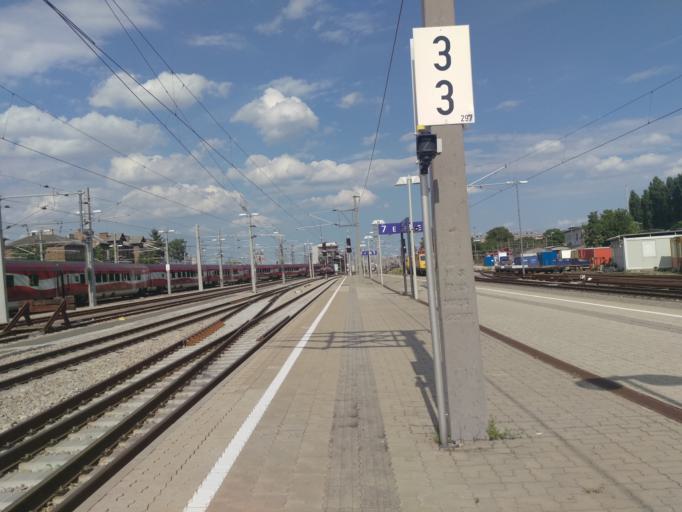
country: AT
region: Vienna
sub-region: Wien Stadt
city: Vienna
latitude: 48.1751
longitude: 16.3381
